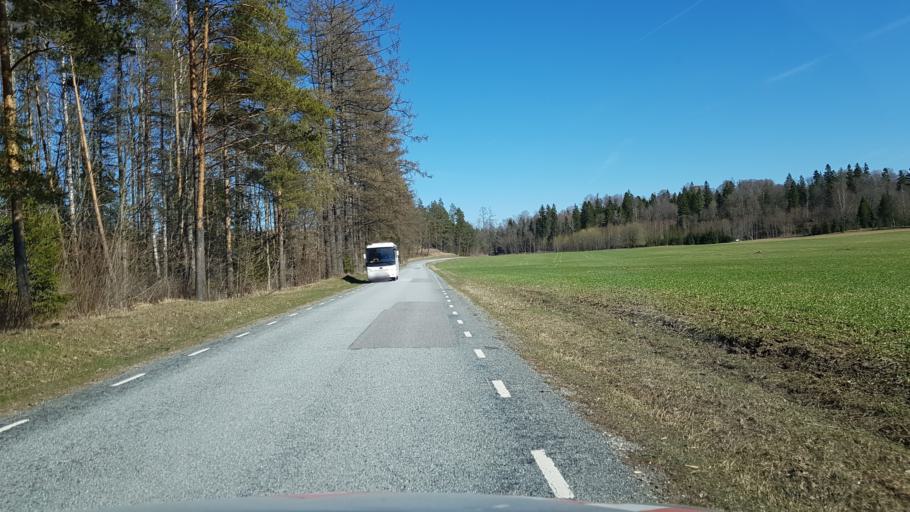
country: EE
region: Laeaene-Virumaa
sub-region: Someru vald
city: Someru
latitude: 59.3314
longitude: 26.5632
